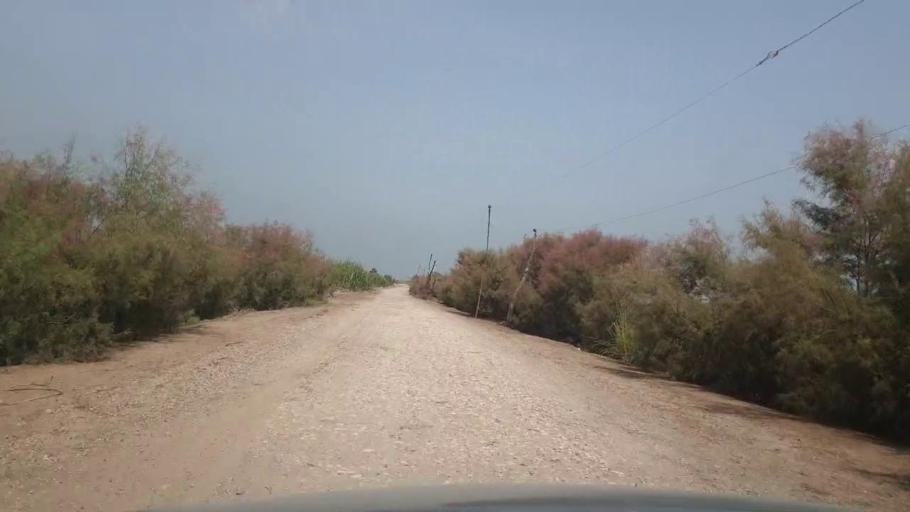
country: PK
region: Sindh
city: Garhi Yasin
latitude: 27.9567
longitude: 68.3643
